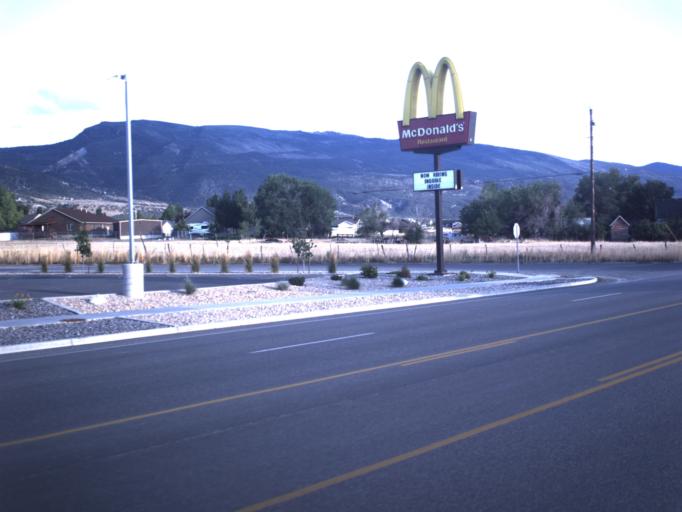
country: US
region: Utah
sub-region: Sanpete County
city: Ephraim
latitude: 39.3502
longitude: -111.5882
